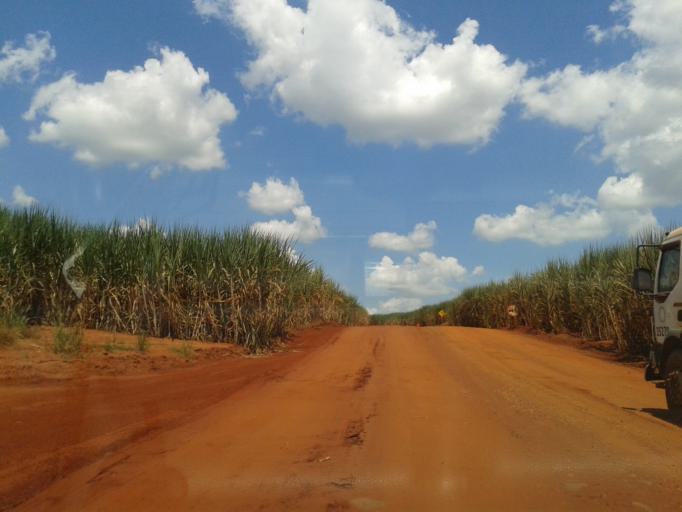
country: BR
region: Minas Gerais
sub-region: Ituiutaba
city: Ituiutaba
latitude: -18.9851
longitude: -49.6633
